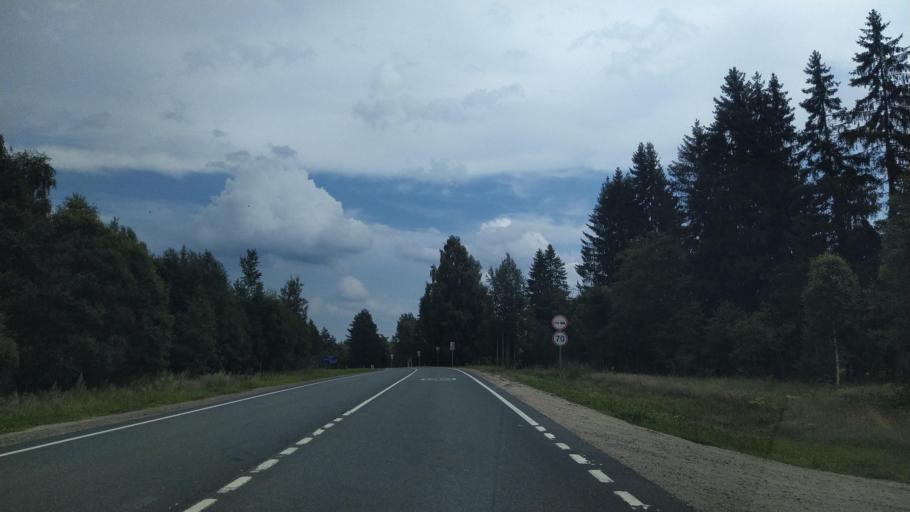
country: RU
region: Pskov
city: Pskov
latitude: 57.8130
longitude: 28.6844
